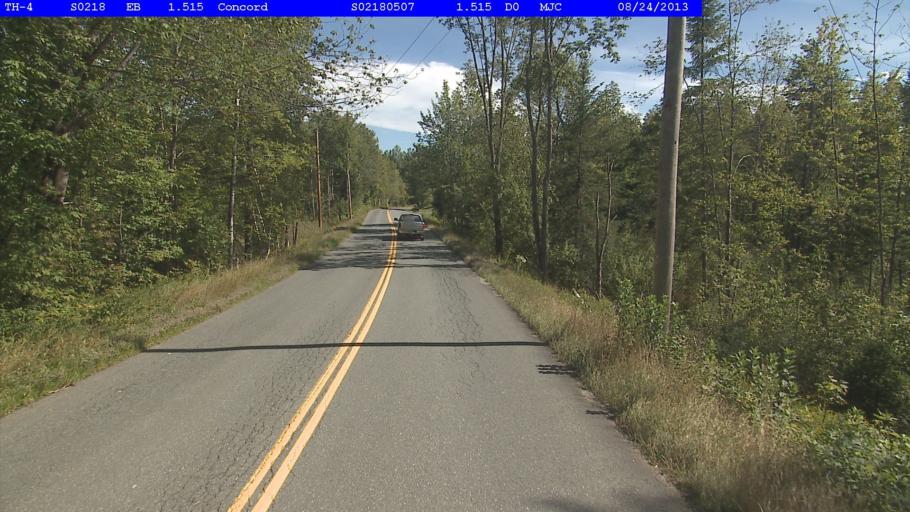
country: US
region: New Hampshire
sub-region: Grafton County
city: Littleton
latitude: 44.4446
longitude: -71.7648
